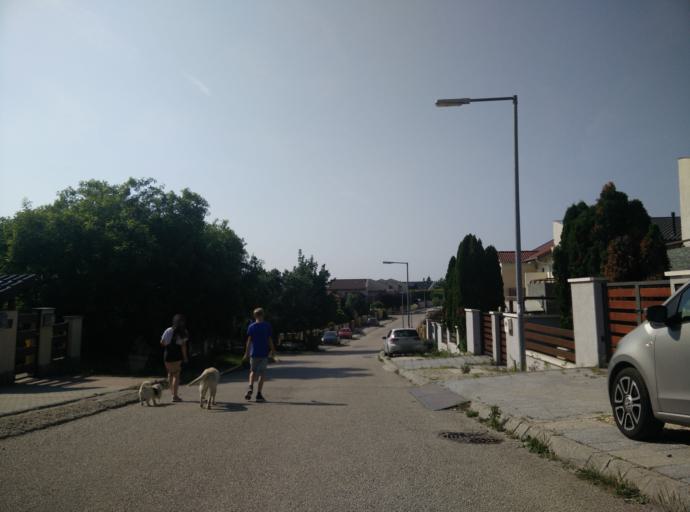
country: HU
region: Pest
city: Biatorbagy
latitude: 47.4775
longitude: 18.8164
